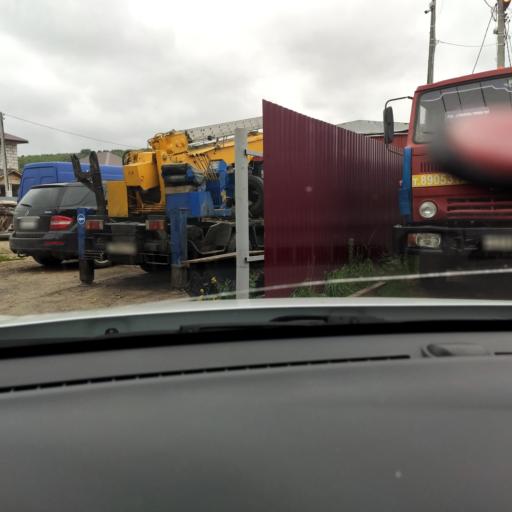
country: RU
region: Tatarstan
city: Stolbishchi
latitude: 55.7480
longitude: 49.3107
